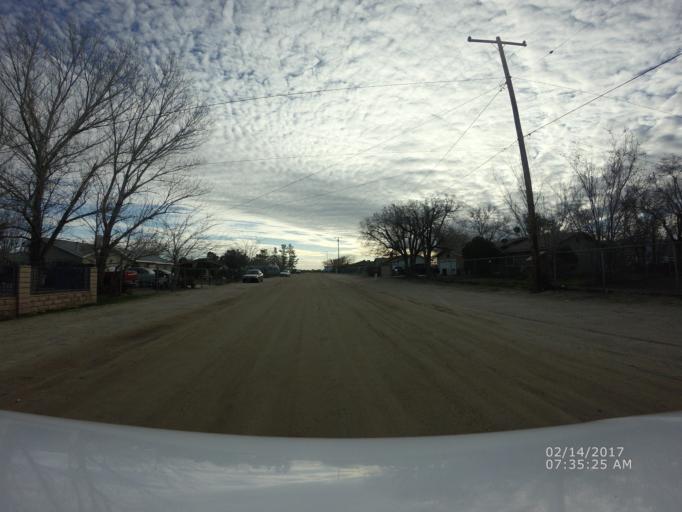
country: US
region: California
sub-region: Los Angeles County
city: Littlerock
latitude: 34.5466
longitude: -117.9424
